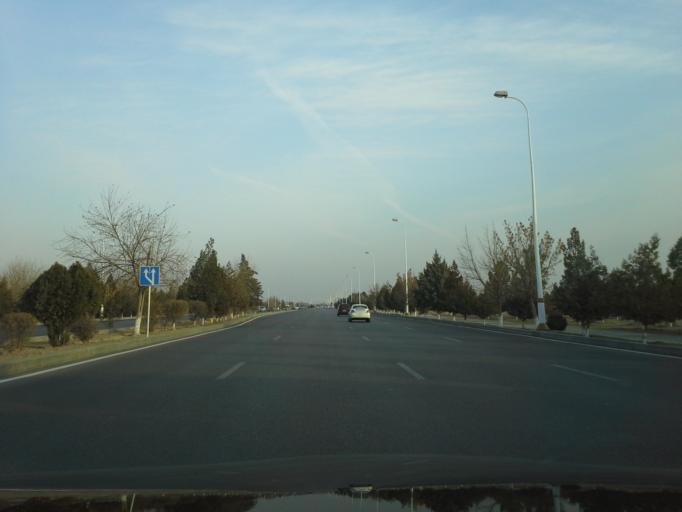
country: TM
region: Ahal
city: Abadan
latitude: 38.0371
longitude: 58.2177
